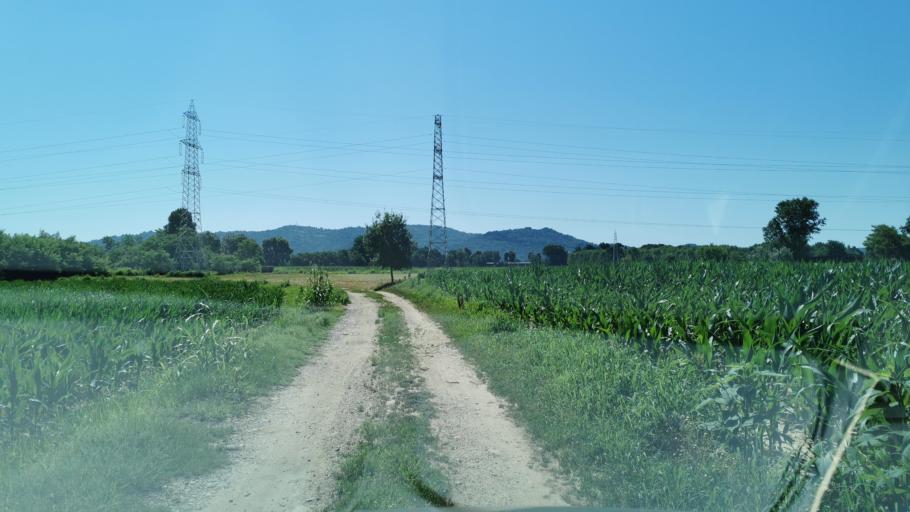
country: IT
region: Piedmont
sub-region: Provincia di Torino
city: Brandizzo
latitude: 45.1933
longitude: 7.8310
